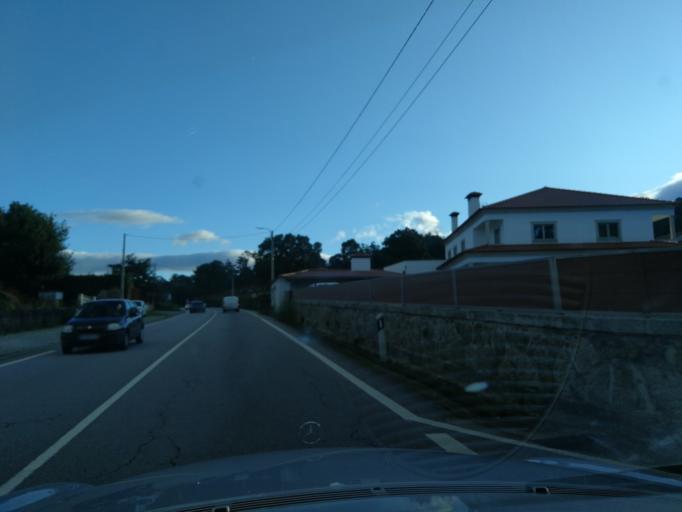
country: PT
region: Braga
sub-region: Esposende
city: Marinhas
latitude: 41.5934
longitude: -8.7376
